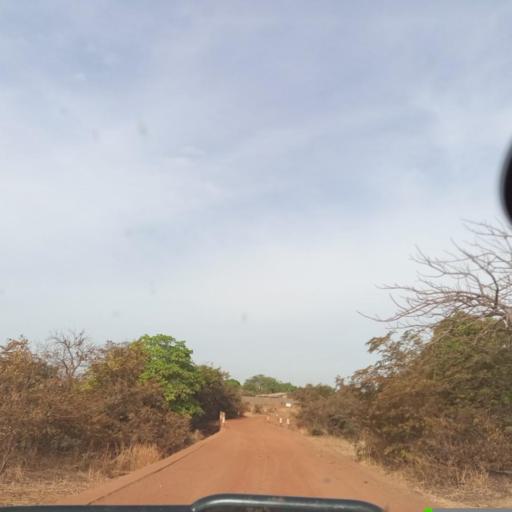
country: ML
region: Koulikoro
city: Koulikoro
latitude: 13.1084
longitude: -7.6485
